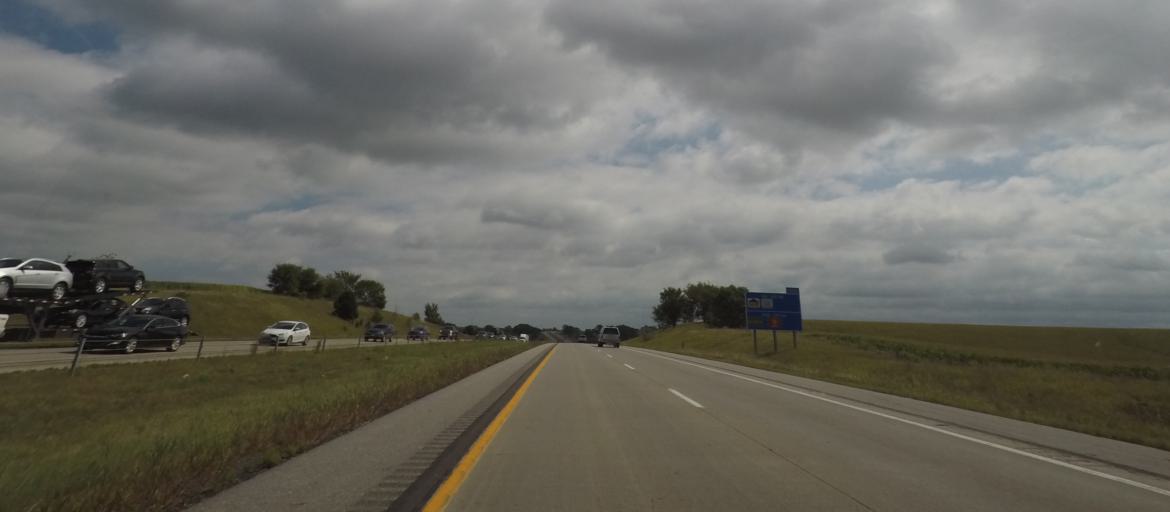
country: US
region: Iowa
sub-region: Jasper County
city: Newton
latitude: 41.6827
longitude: -93.1355
